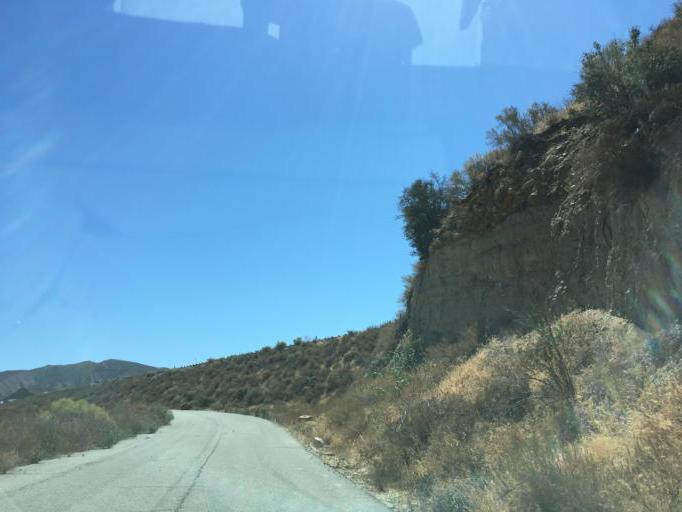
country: US
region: California
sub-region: Los Angeles County
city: Agua Dulce
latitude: 34.4367
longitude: -118.3770
